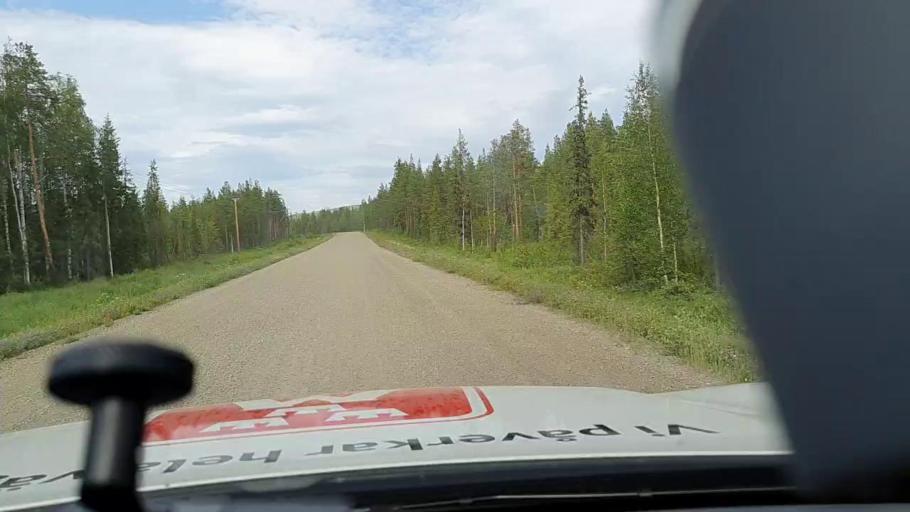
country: SE
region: Norrbotten
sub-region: Alvsbyns Kommun
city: AElvsbyn
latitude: 66.1401
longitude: 21.0108
